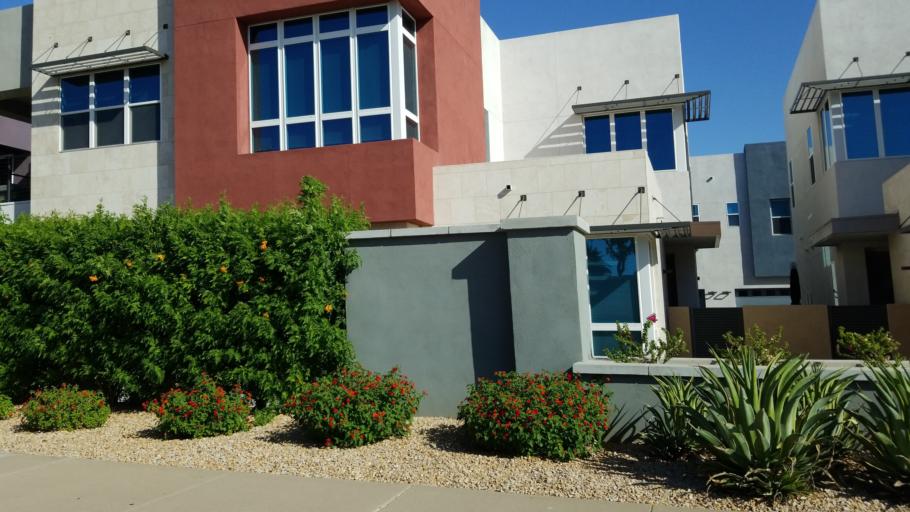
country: US
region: Arizona
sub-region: Maricopa County
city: Scottsdale
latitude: 33.5719
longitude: -111.8856
